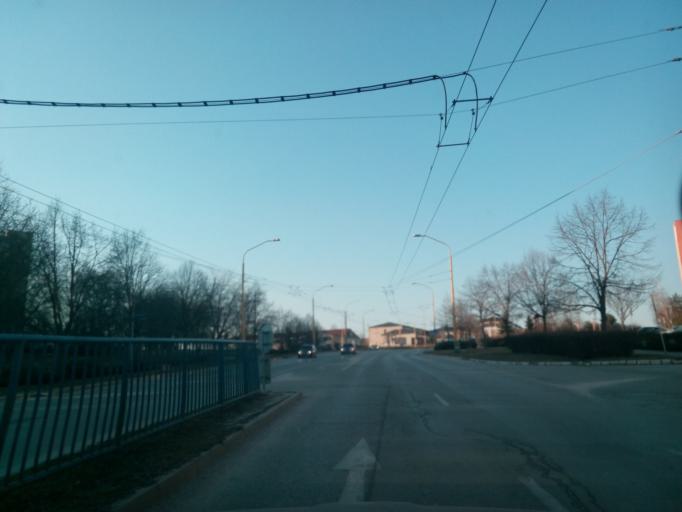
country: SK
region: Kosicky
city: Kosice
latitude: 48.7171
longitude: 21.2144
